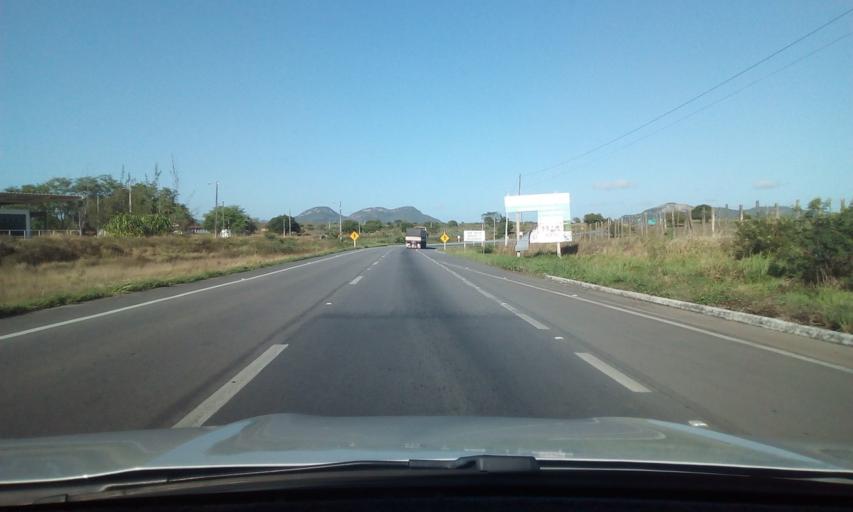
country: BR
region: Paraiba
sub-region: Gurinhem
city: Gurinhem
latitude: -7.1661
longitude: -35.3557
